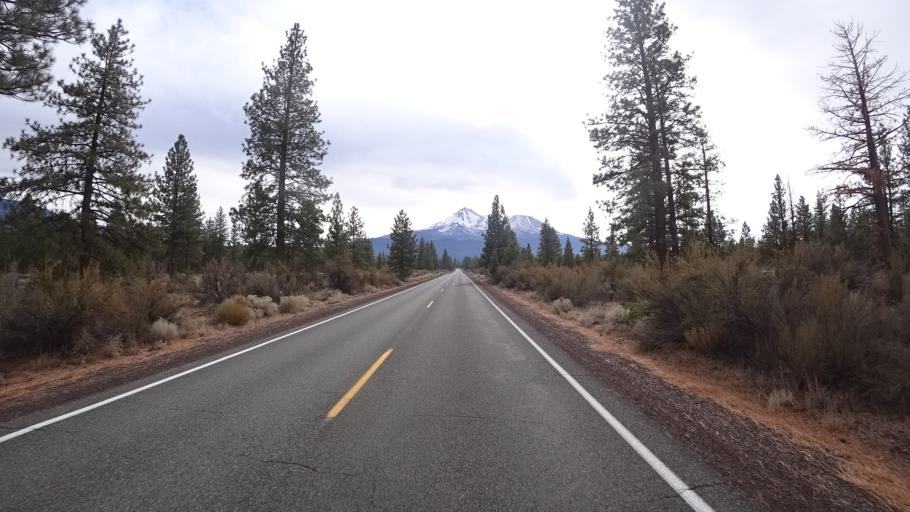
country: US
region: California
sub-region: Siskiyou County
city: Weed
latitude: 41.5441
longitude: -122.2467
